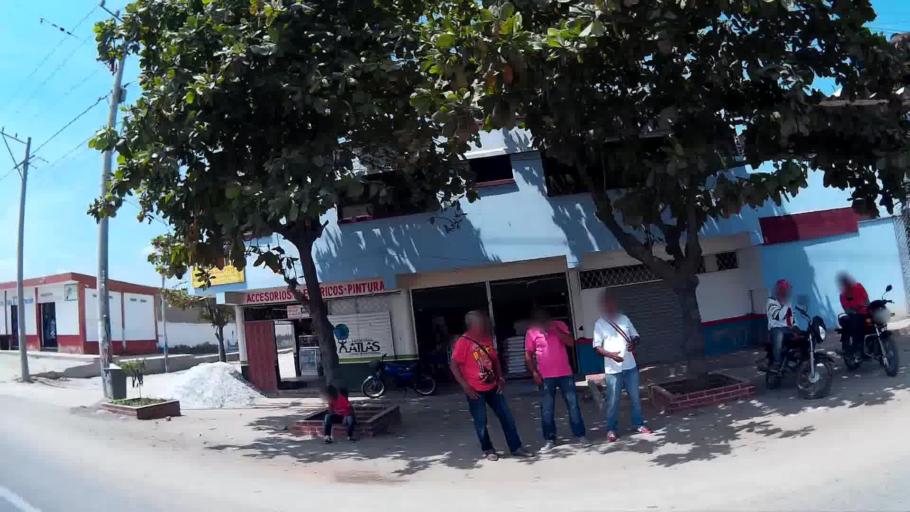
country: CO
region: Magdalena
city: Cienaga
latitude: 11.0054
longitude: -74.2389
